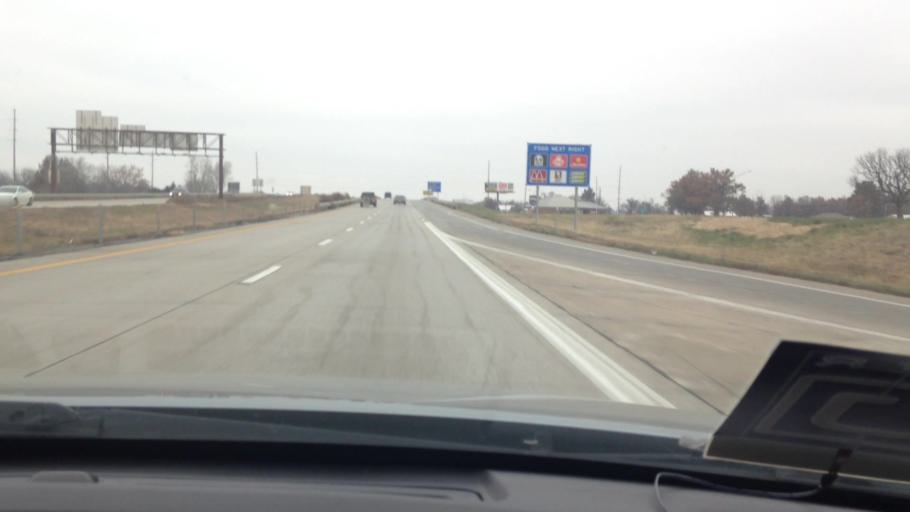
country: US
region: Missouri
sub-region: Cass County
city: Harrisonville
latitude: 38.6515
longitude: -94.3652
